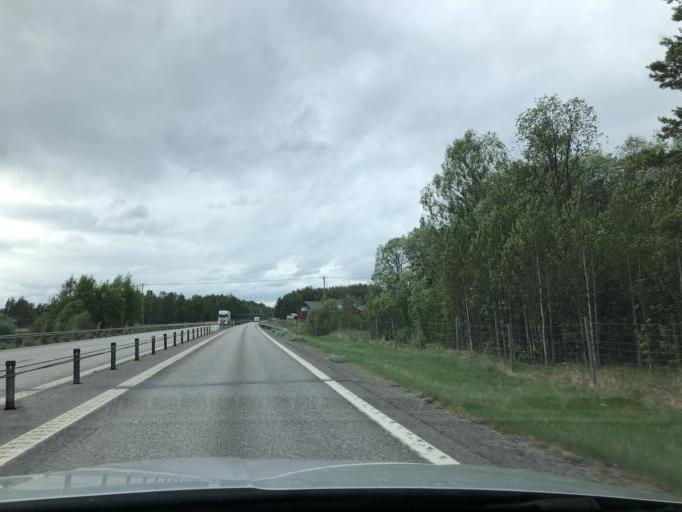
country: SE
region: Norrbotten
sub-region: Pitea Kommun
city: Bergsviken
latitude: 65.2969
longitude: 21.4207
